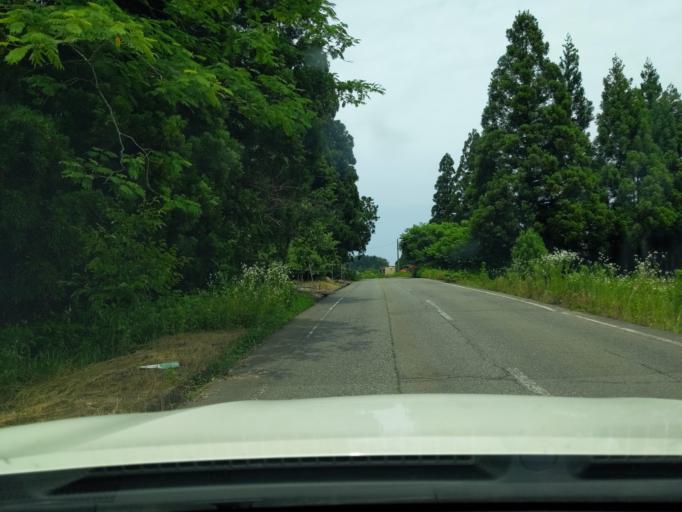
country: JP
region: Niigata
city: Kashiwazaki
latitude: 37.3402
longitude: 138.5533
